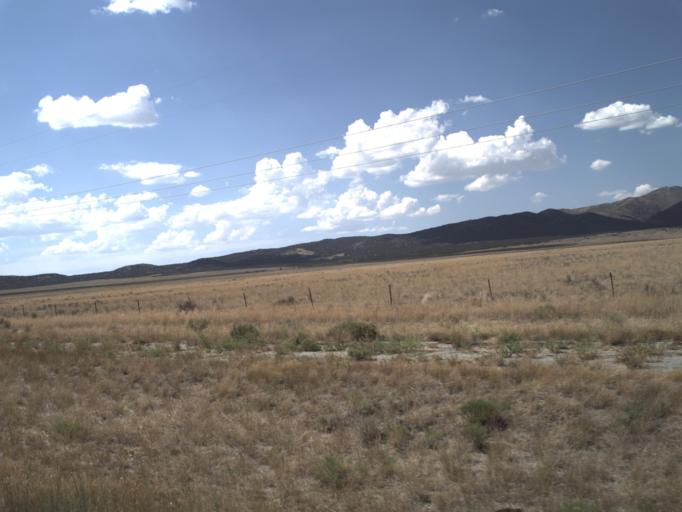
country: US
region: Idaho
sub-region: Power County
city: American Falls
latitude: 41.9681
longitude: -113.0943
